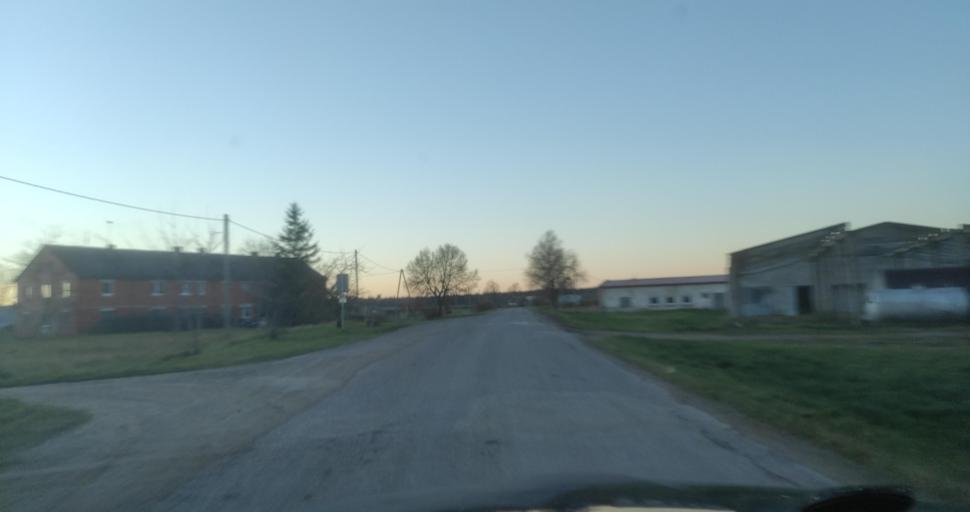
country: LV
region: Dundaga
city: Dundaga
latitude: 57.3756
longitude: 22.2293
